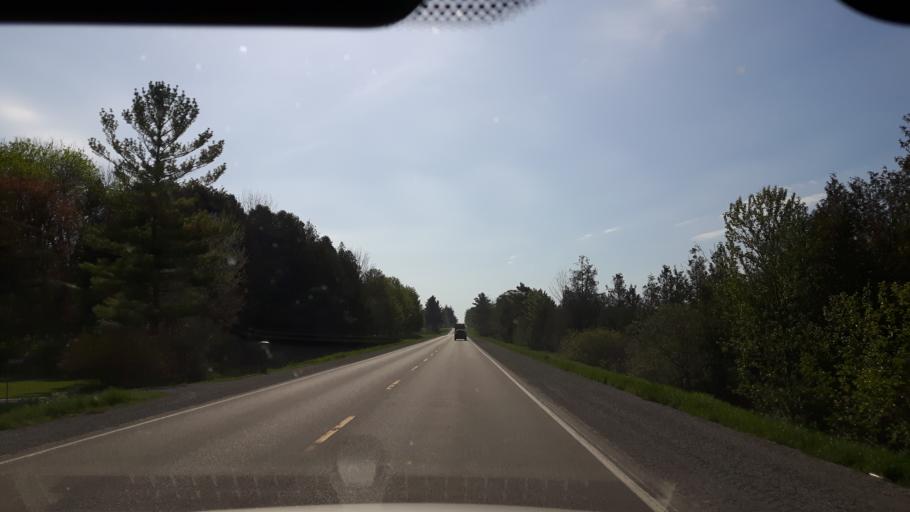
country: CA
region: Ontario
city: Bluewater
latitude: 43.5538
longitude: -81.6785
